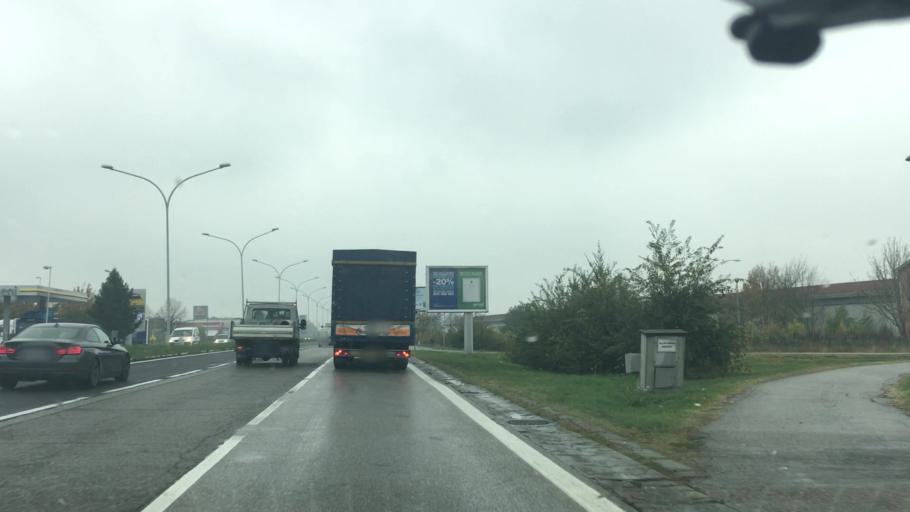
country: IT
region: Emilia-Romagna
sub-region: Provincia di Bologna
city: Casalecchio di Reno
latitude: 44.5118
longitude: 11.2730
